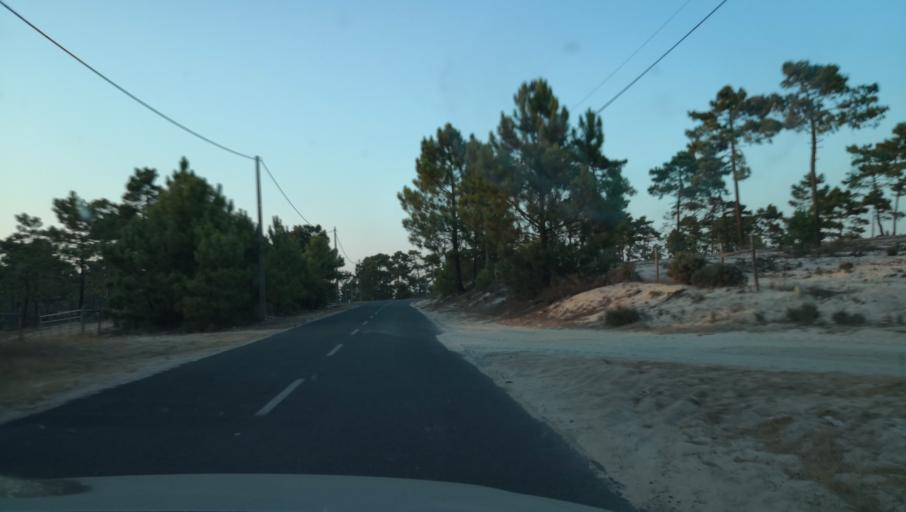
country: PT
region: Setubal
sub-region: Setubal
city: Setubal
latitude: 38.3842
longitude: -8.7829
